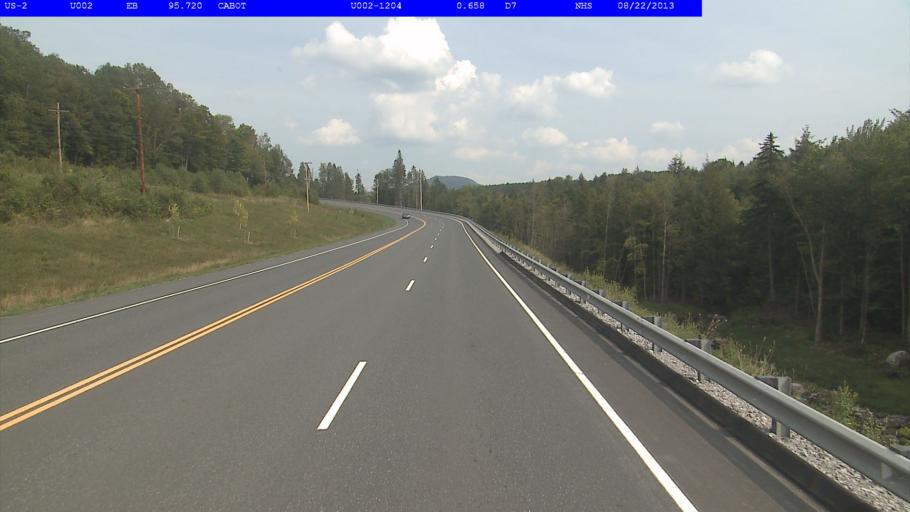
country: US
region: Vermont
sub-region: Caledonia County
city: Hardwick
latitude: 44.3628
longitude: -72.3116
